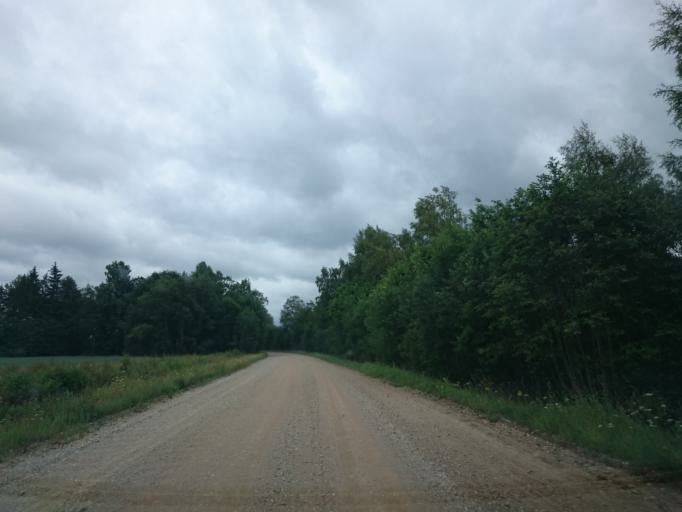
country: LV
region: Pavilostas
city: Pavilosta
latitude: 56.7688
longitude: 21.2603
